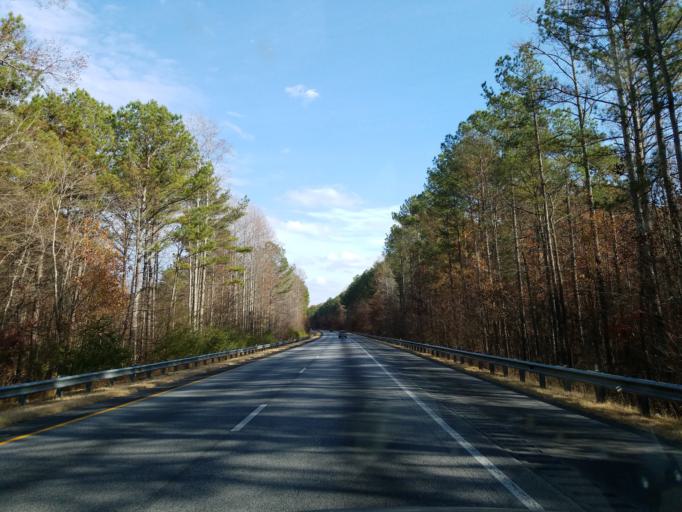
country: US
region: Alabama
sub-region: Cleburne County
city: Heflin
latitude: 33.6186
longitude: -85.6449
